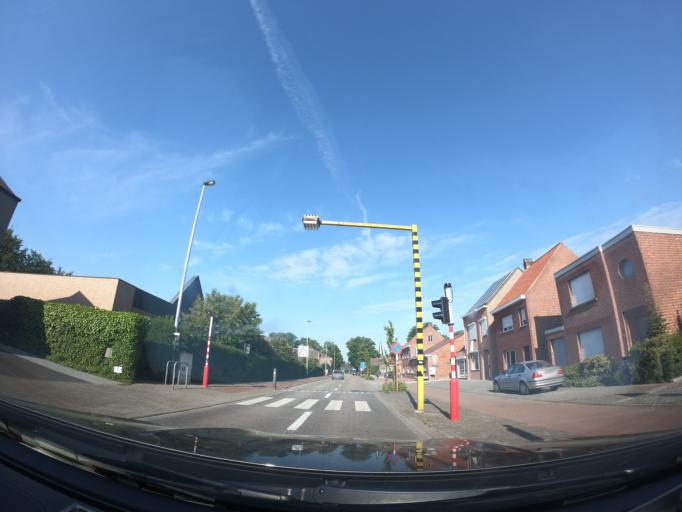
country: BE
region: Flanders
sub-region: Provincie Antwerpen
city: Olen
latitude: 51.1443
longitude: 4.8622
